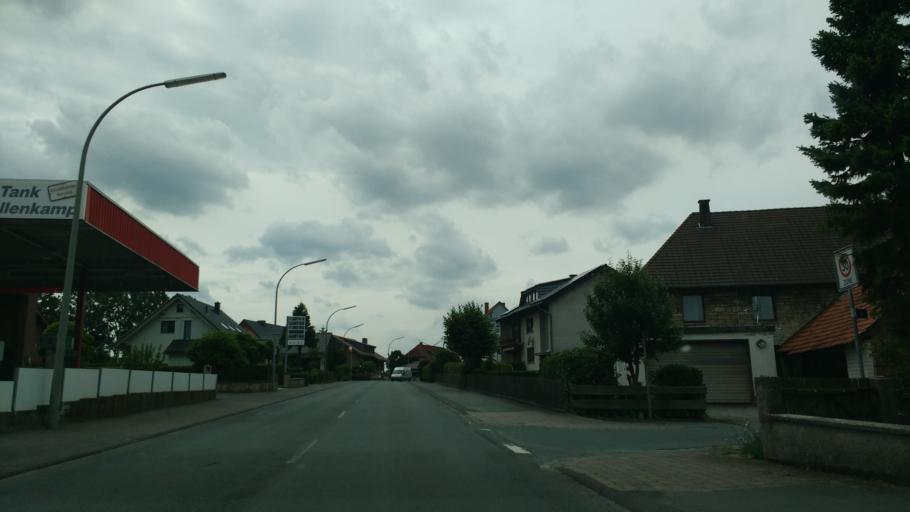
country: DE
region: North Rhine-Westphalia
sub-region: Regierungsbezirk Detmold
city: Wunnenberg
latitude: 51.5637
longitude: 8.7253
